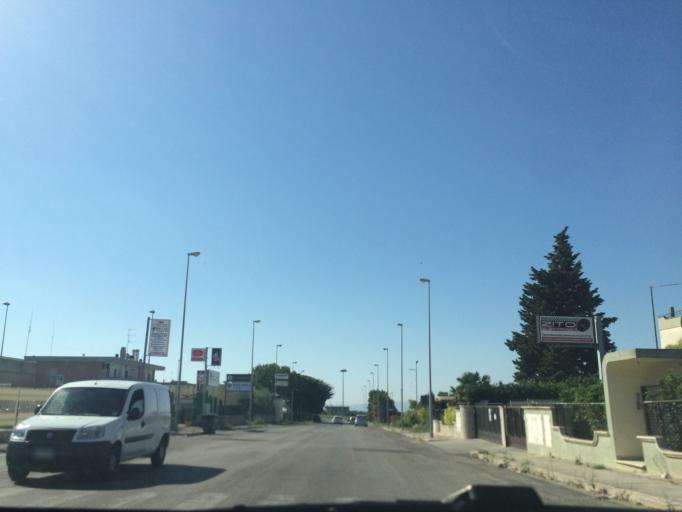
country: IT
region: Basilicate
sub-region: Provincia di Matera
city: Matera
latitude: 40.6713
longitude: 16.5732
